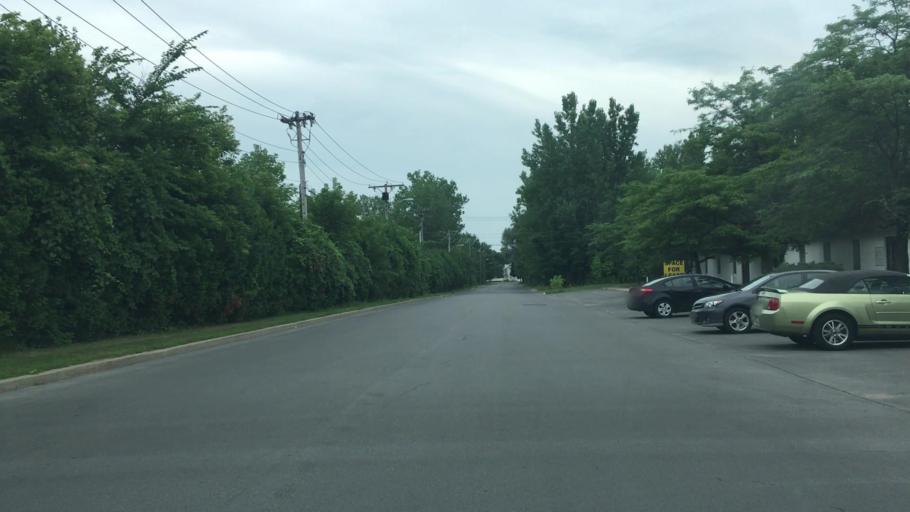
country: US
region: New York
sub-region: Clinton County
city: Plattsburgh West
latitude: 44.6958
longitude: -73.4830
